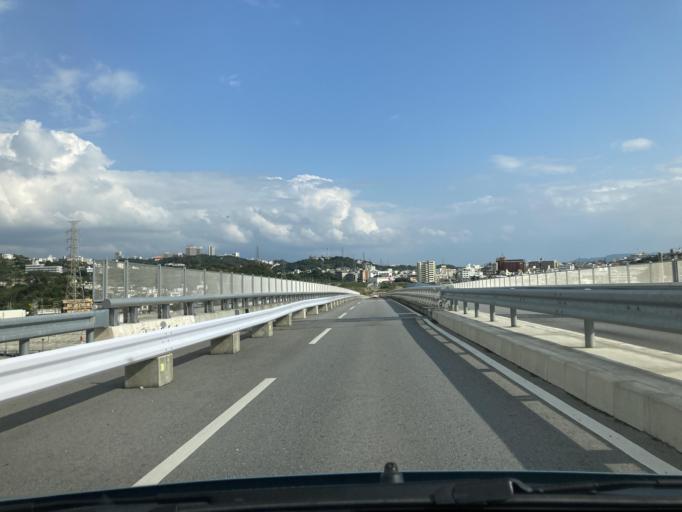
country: JP
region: Okinawa
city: Ginowan
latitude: 26.2422
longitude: 127.7397
